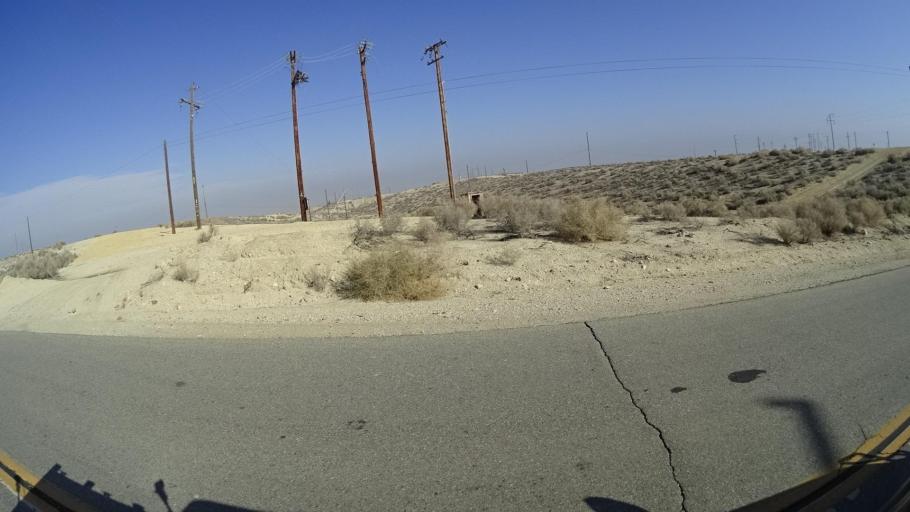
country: US
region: California
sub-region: Kern County
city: Taft Heights
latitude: 35.1446
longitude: -119.5120
